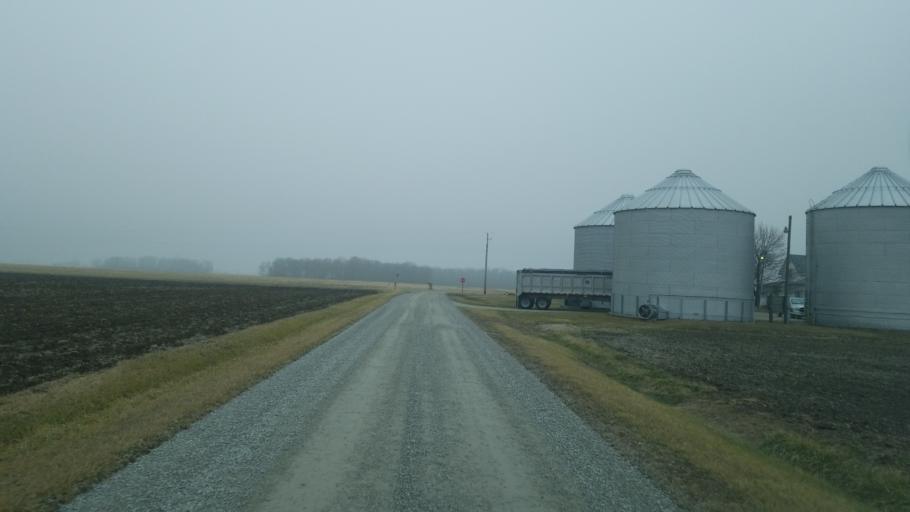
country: US
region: Indiana
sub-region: Adams County
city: Berne
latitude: 40.6398
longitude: -85.0700
